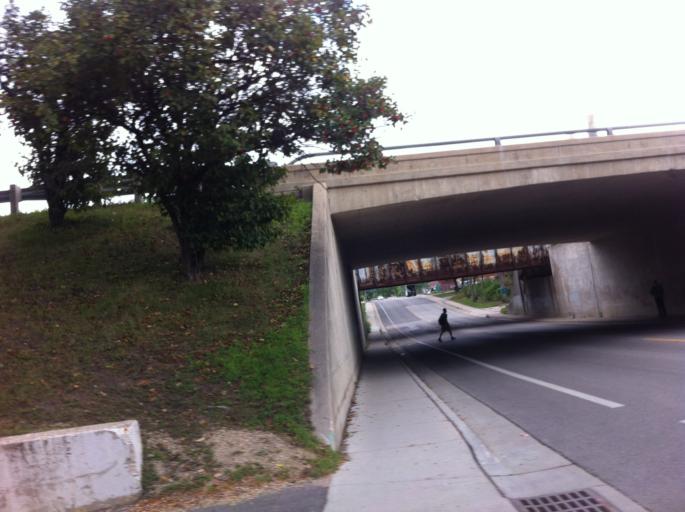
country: US
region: Wisconsin
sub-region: Dane County
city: Shorewood Hills
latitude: 43.0730
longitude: -89.4253
